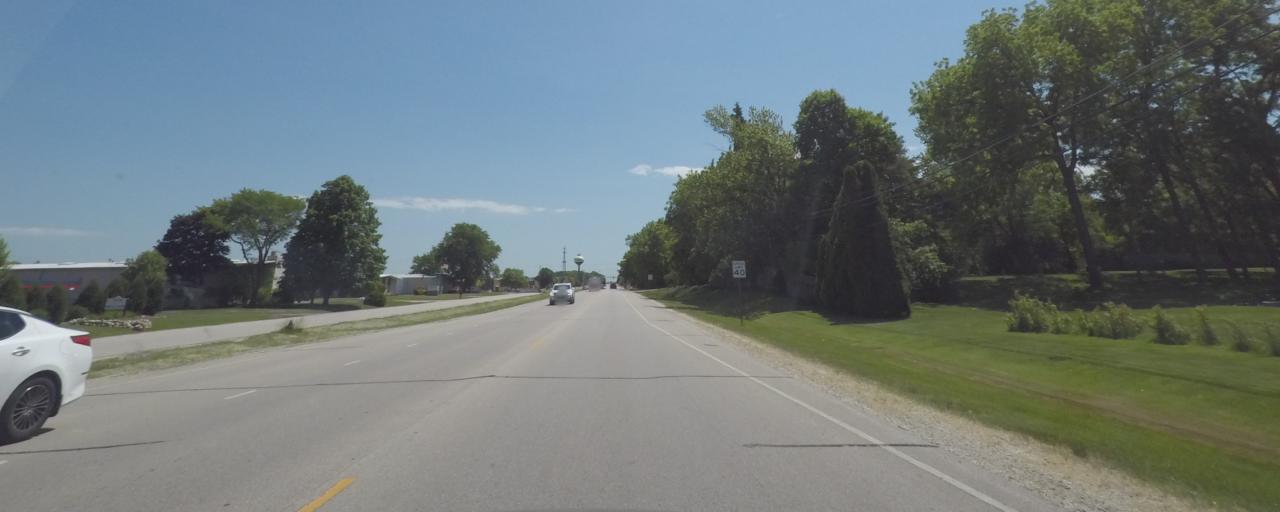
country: US
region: Wisconsin
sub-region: Waukesha County
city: New Berlin
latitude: 43.0064
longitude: -88.1274
